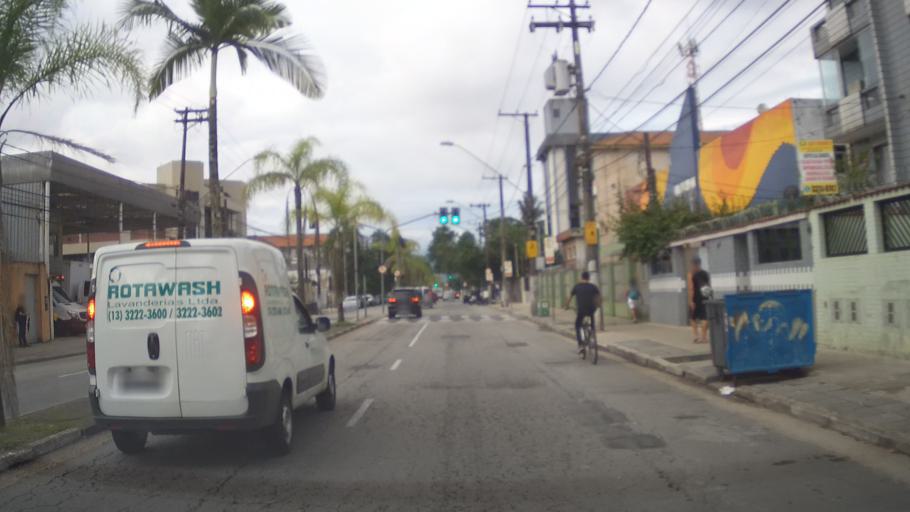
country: BR
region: Sao Paulo
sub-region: Santos
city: Santos
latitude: -23.9454
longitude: -46.3216
